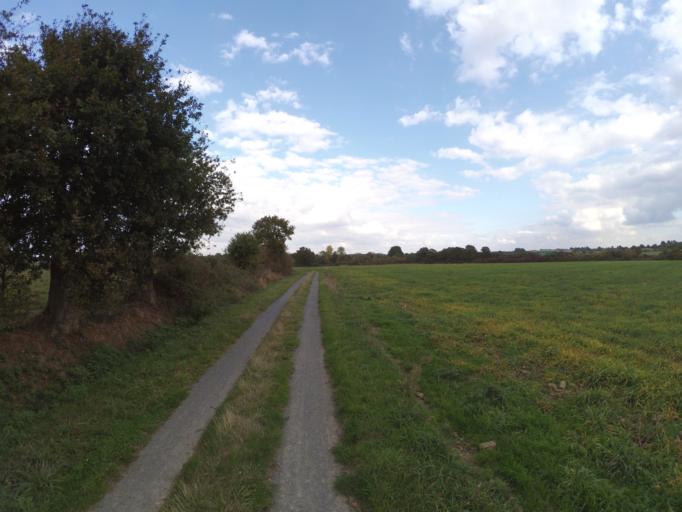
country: FR
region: Pays de la Loire
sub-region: Departement de la Loire-Atlantique
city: Saint-Lumine-de-Clisson
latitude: 47.0749
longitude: -1.3397
